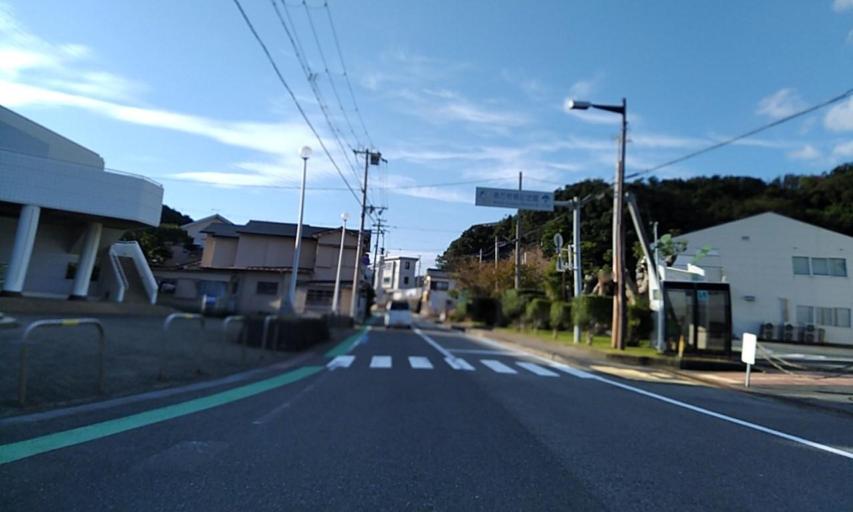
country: JP
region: Wakayama
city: Tanabe
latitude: 33.6927
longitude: 135.3549
